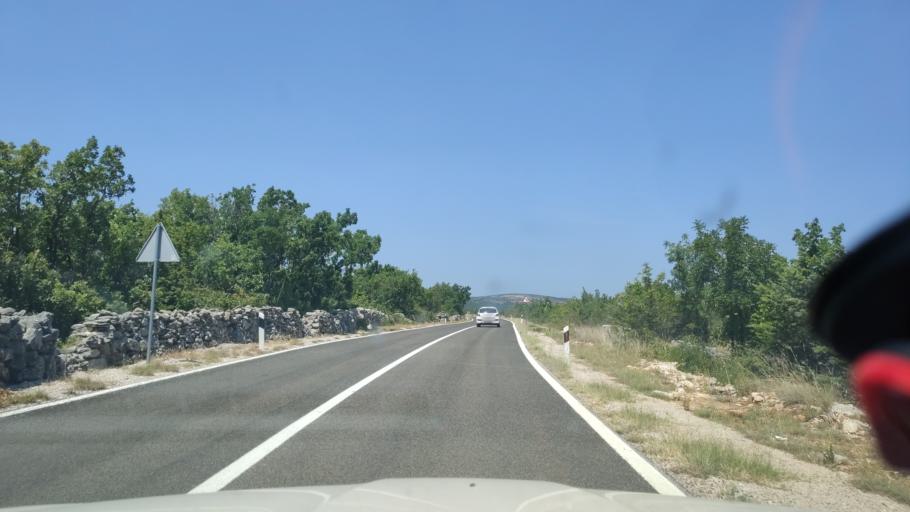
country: HR
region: Sibensko-Kniniska
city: Kistanje
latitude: 43.9711
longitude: 15.9010
